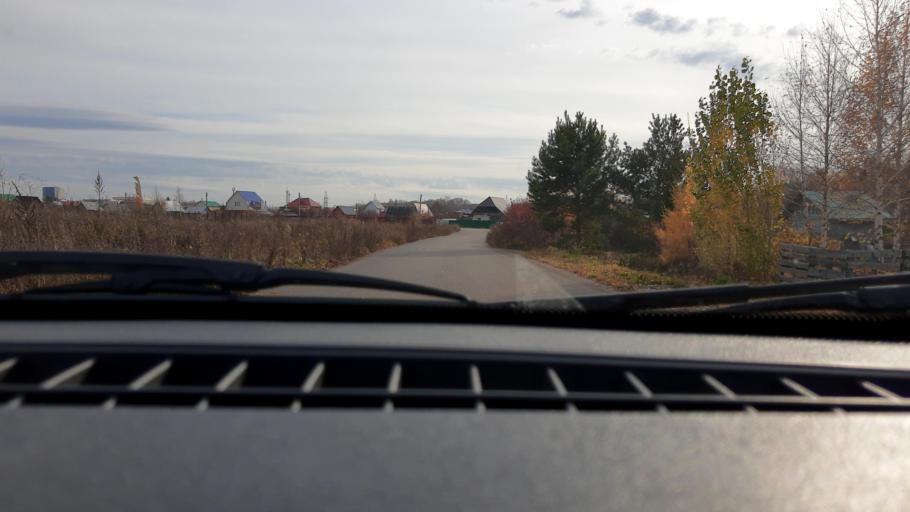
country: RU
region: Bashkortostan
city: Ufa
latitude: 54.5965
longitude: 55.8987
